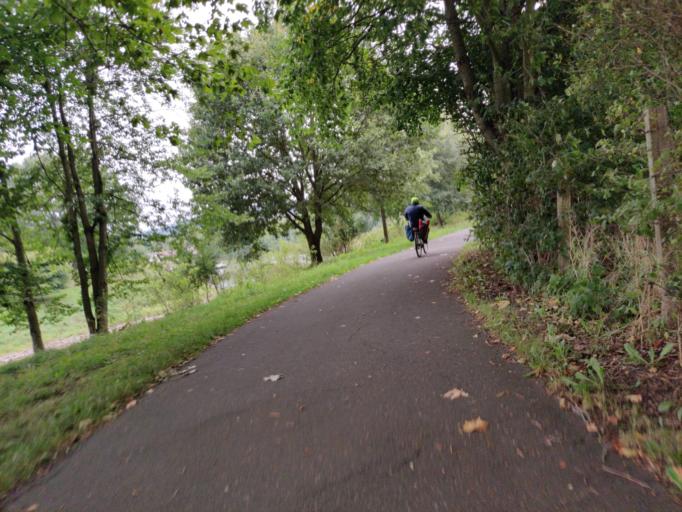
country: DE
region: North Rhine-Westphalia
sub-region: Regierungsbezirk Detmold
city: Hoexter
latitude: 51.7744
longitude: 9.4039
